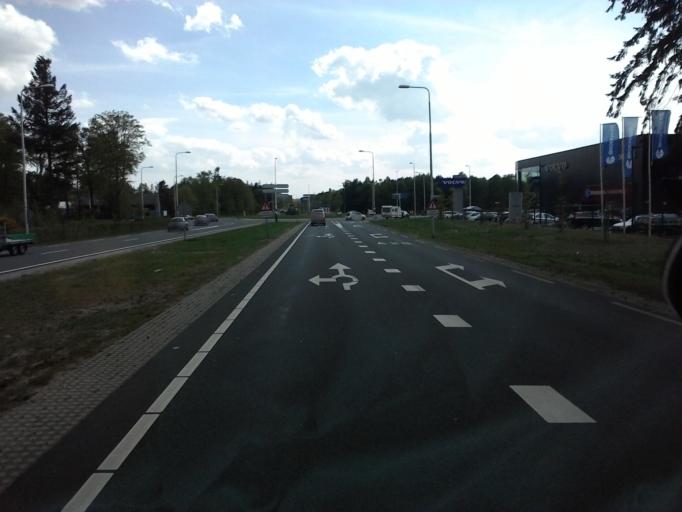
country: NL
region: Utrecht
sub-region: Gemeente Zeist
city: Zeist
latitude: 52.1101
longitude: 5.2612
